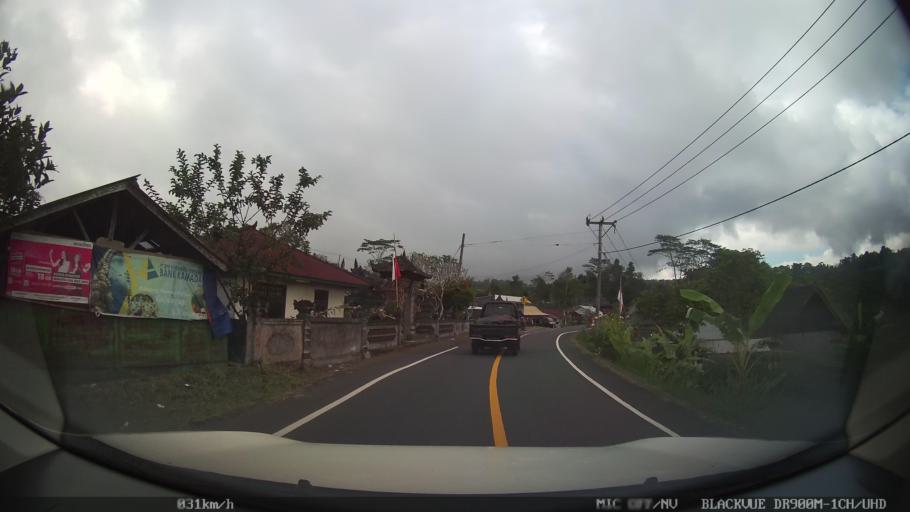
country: ID
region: Bali
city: Banjar Bias
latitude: -8.3297
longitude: 115.4047
